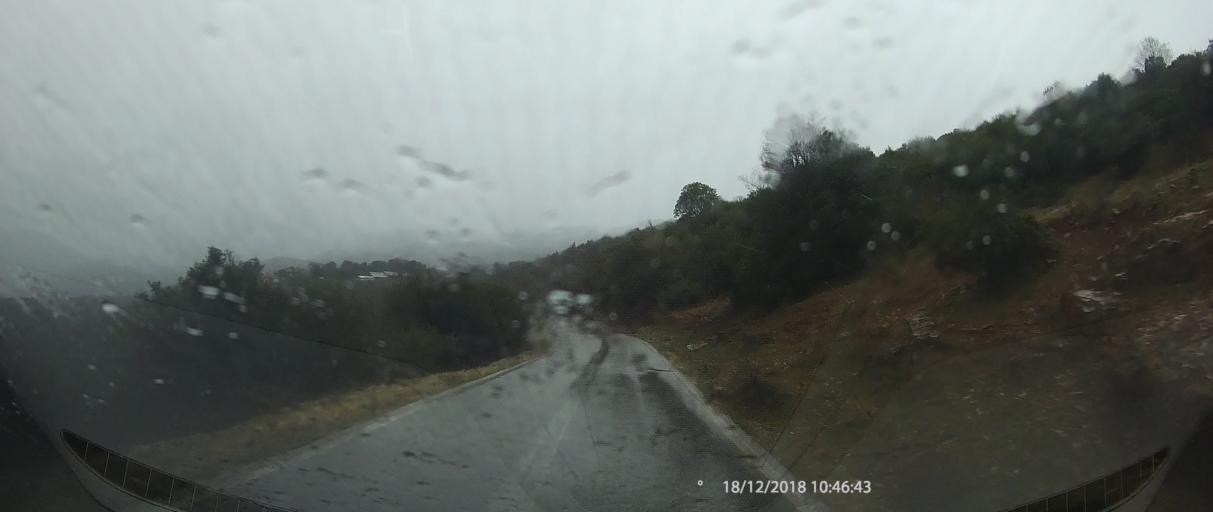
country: GR
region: Central Macedonia
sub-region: Nomos Pierias
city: Kato Milia
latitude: 40.1860
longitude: 22.3253
